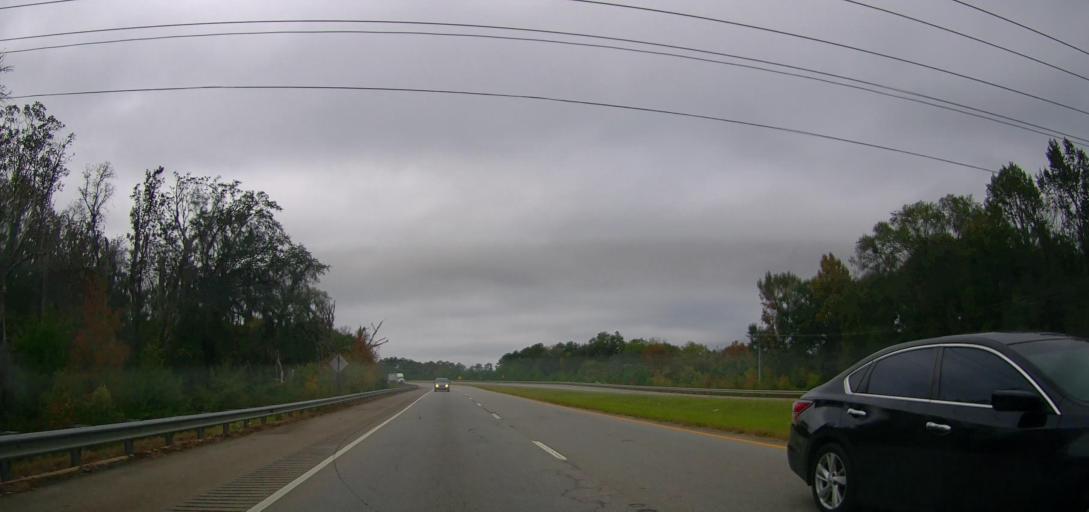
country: US
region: Georgia
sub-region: Thomas County
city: Thomasville
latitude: 30.8749
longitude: -83.9795
